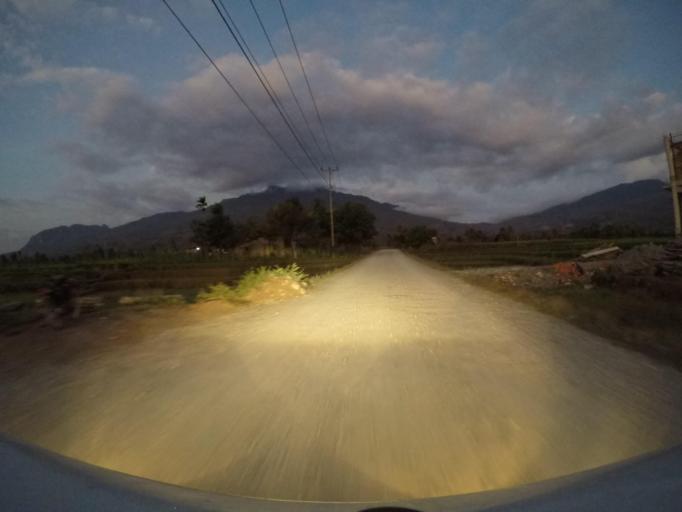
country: TL
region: Bobonaro
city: Maliana
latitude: -8.9807
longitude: 125.2146
